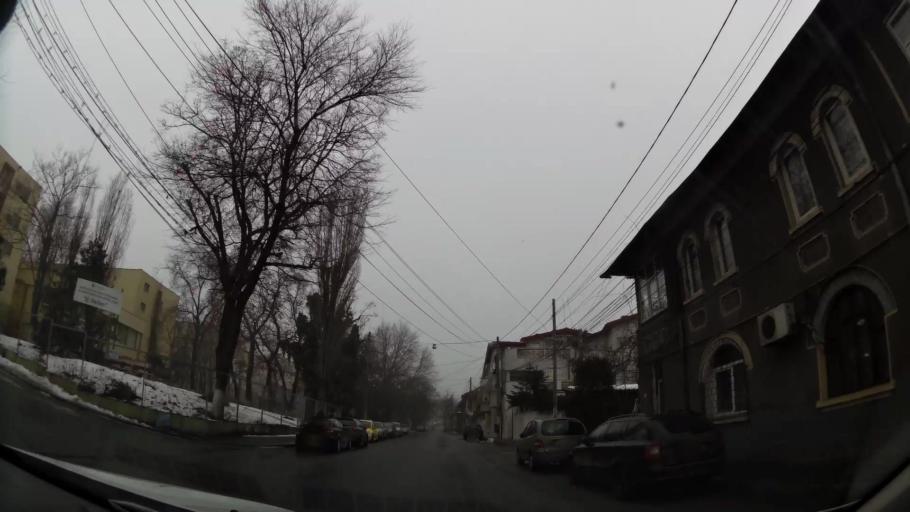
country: RO
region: Ilfov
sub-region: Comuna Chiajna
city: Rosu
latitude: 44.4492
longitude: 26.0555
